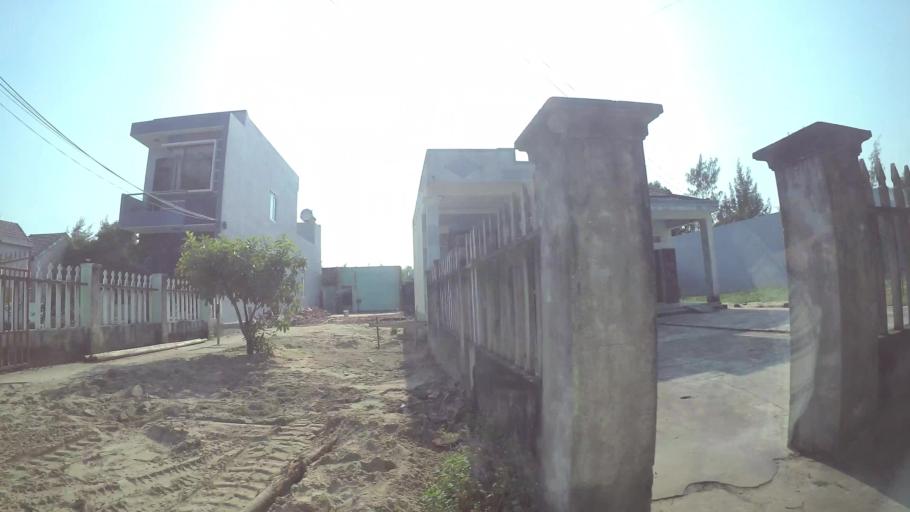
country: VN
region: Da Nang
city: Ngu Hanh Son
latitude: 15.9547
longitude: 108.2655
